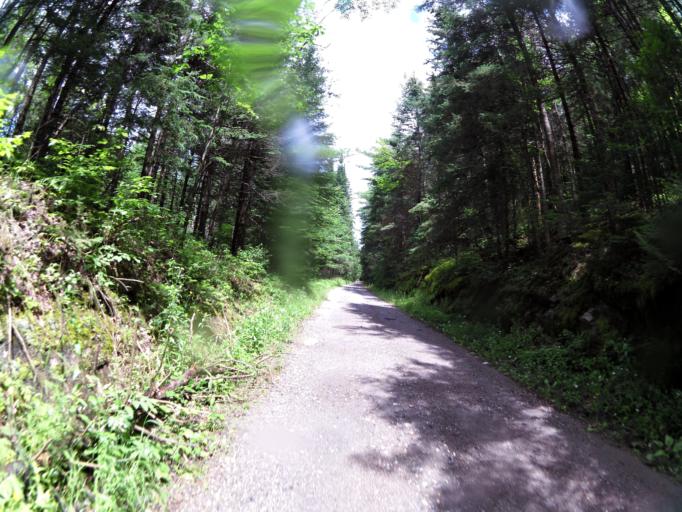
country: CA
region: Ontario
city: Renfrew
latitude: 45.0914
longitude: -76.7190
